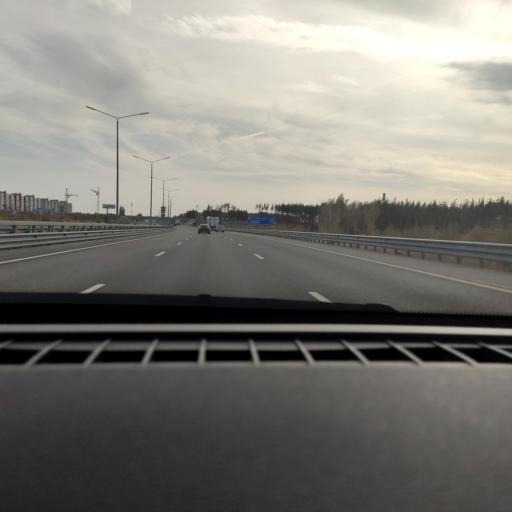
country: RU
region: Voronezj
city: Somovo
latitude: 51.7474
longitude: 39.3057
